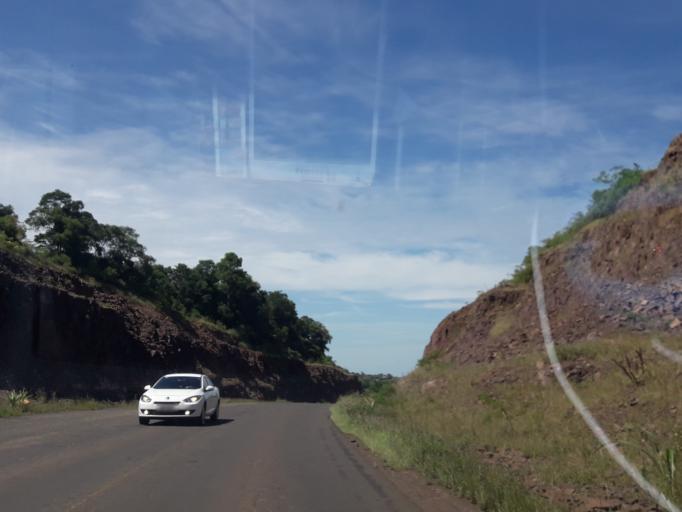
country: AR
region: Misiones
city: Bernardo de Irigoyen
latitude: -26.5725
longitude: -53.5108
